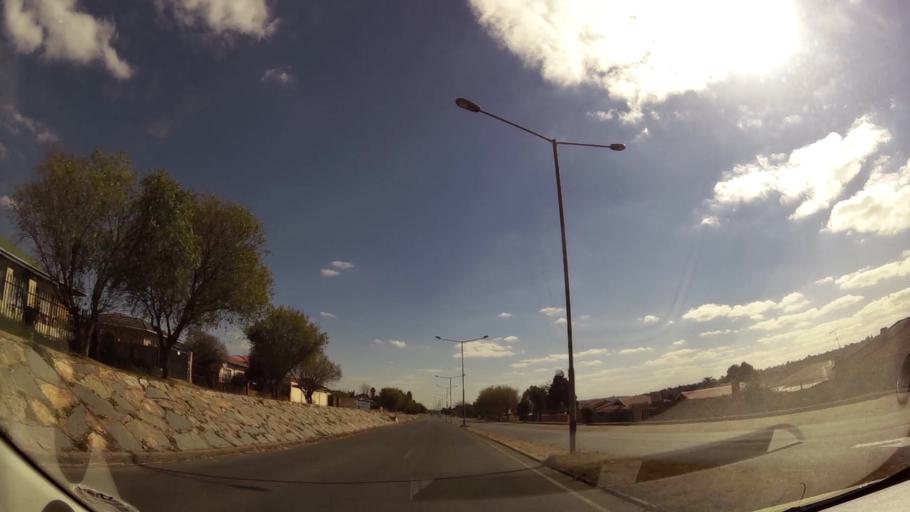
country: ZA
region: Gauteng
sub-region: West Rand District Municipality
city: Krugersdorp
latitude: -26.1135
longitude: 27.7948
